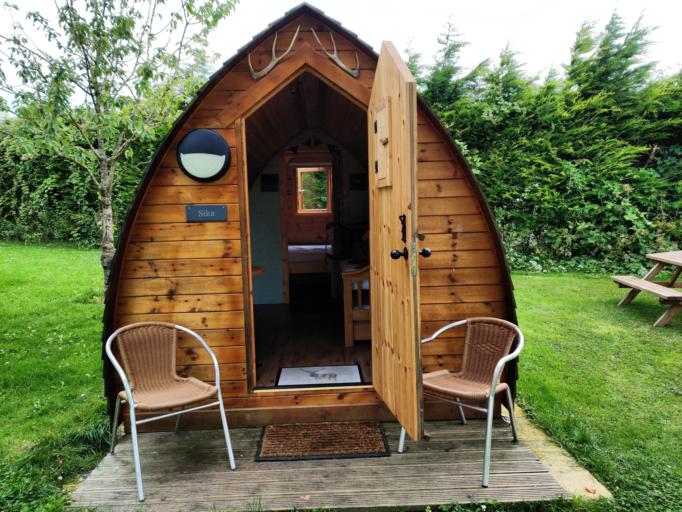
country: GB
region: England
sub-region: Dorset
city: Wareham
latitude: 50.6437
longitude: -2.1002
